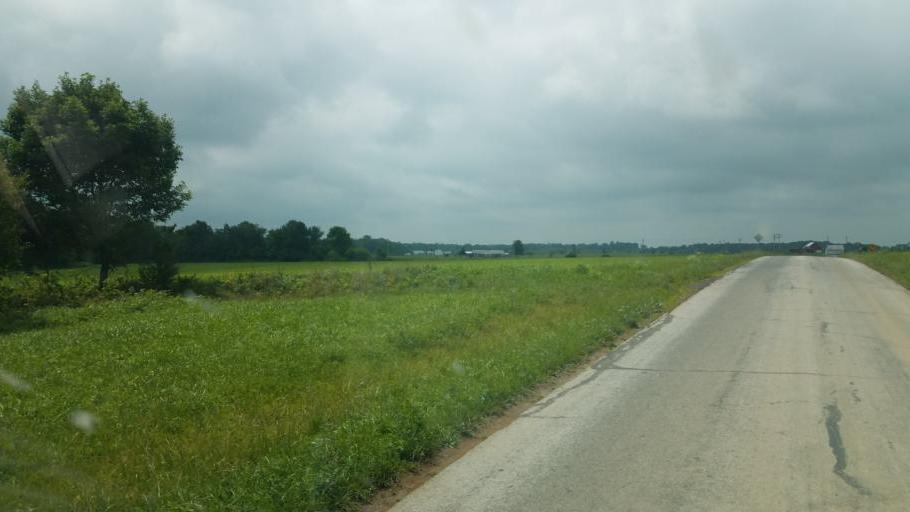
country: US
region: Ohio
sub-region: Highland County
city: Leesburg
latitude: 39.2381
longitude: -83.4875
